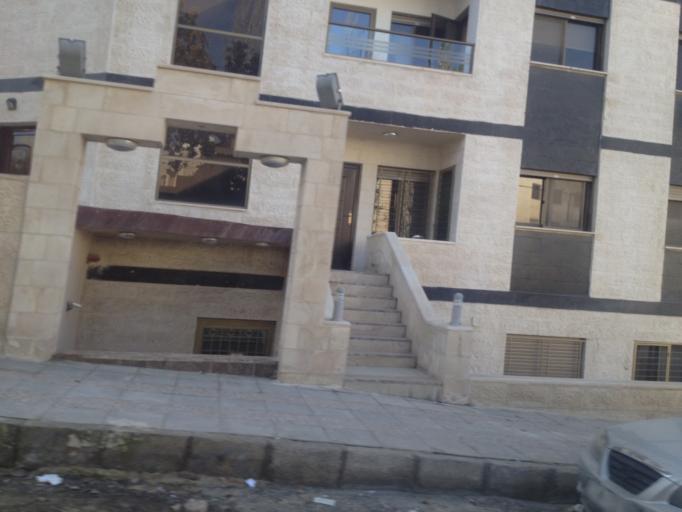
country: JO
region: Amman
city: Wadi as Sir
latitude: 31.9458
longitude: 35.8561
